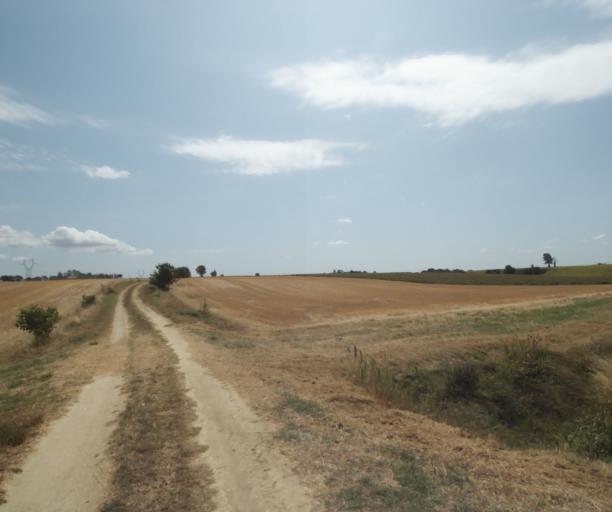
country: FR
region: Midi-Pyrenees
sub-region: Departement de la Haute-Garonne
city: Saint-Felix-Lauragais
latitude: 43.4156
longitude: 1.8961
